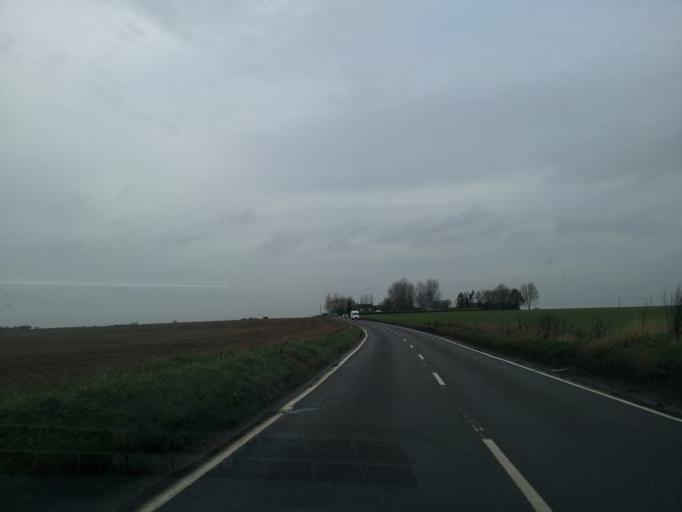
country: GB
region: England
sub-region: Norfolk
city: Martham
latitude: 52.6823
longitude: 1.5951
